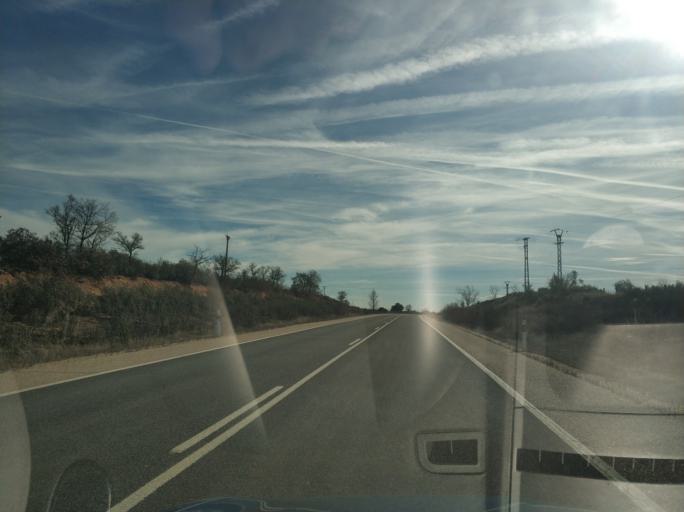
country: ES
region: Castille and Leon
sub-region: Provincia de Salamanca
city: Topas
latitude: 41.1832
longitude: -5.6948
